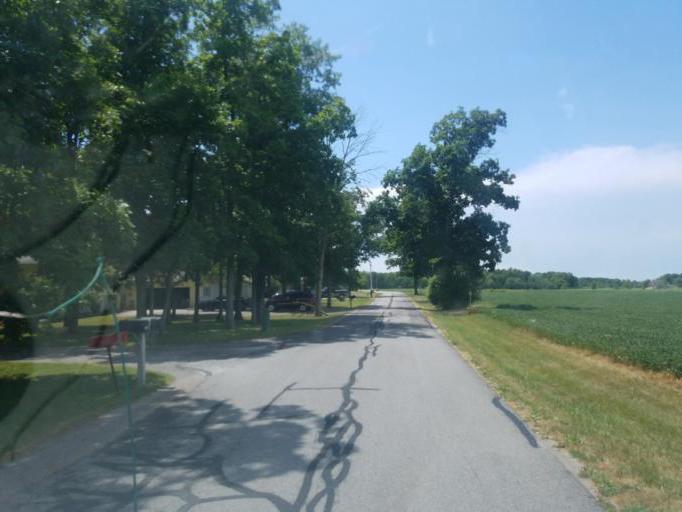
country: US
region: Ohio
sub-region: Paulding County
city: Antwerp
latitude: 41.1752
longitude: -84.7974
